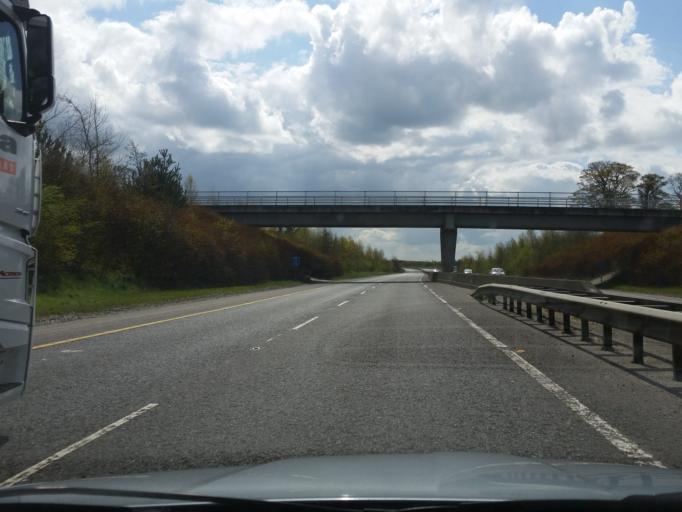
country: IE
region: Leinster
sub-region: An Mhi
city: Ashbourne
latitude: 53.5177
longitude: -6.4197
